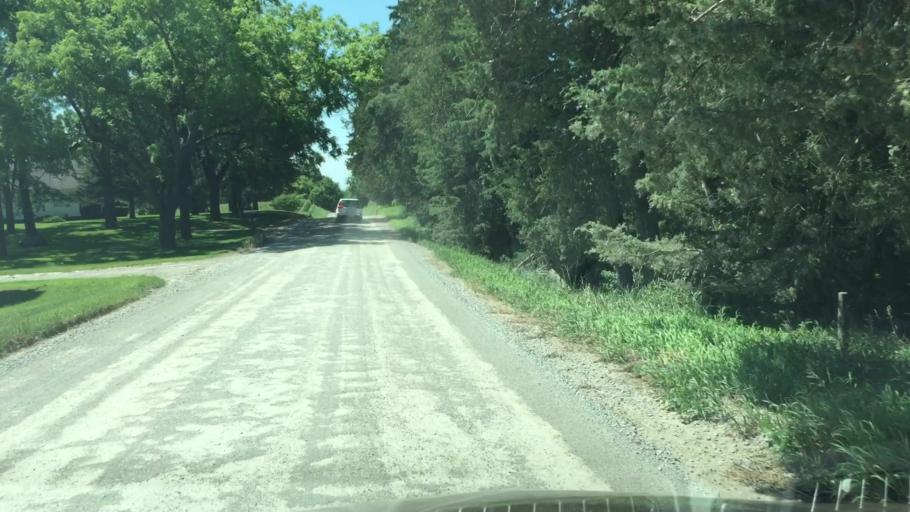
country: US
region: Iowa
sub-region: Linn County
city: Ely
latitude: 41.8240
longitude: -91.5897
